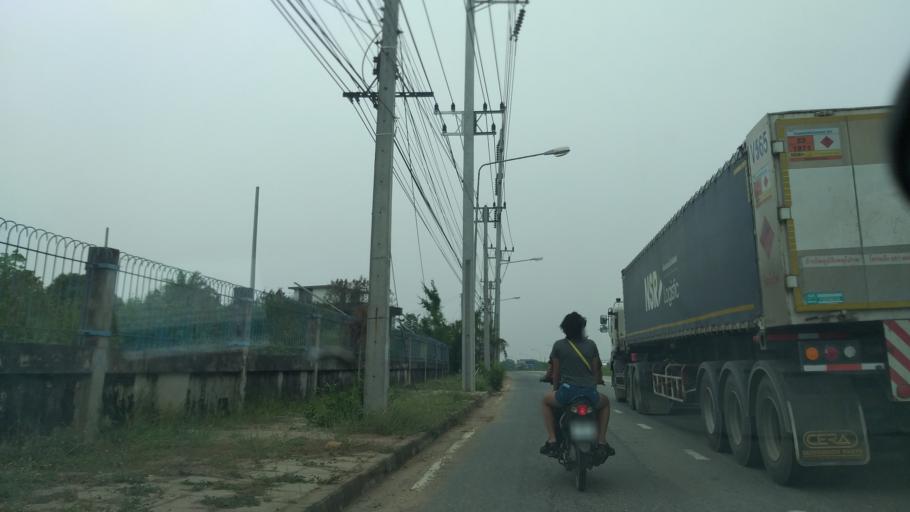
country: TH
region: Chon Buri
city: Ko Chan
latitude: 13.4749
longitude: 101.2837
